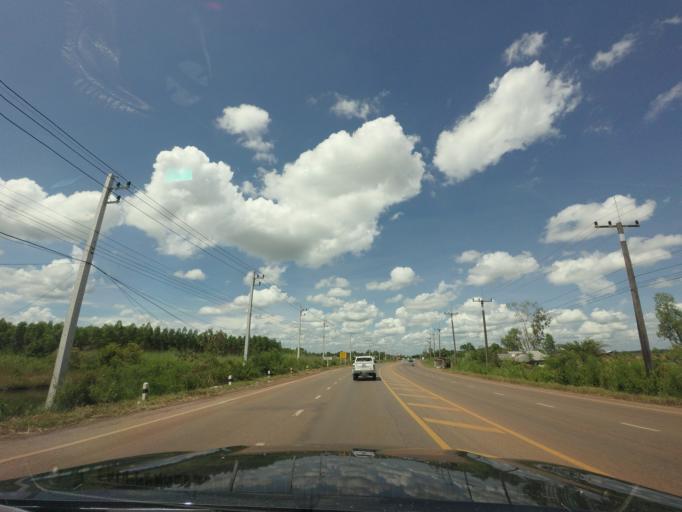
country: TH
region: Changwat Udon Thani
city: Ban Dung
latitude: 17.7216
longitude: 103.2501
